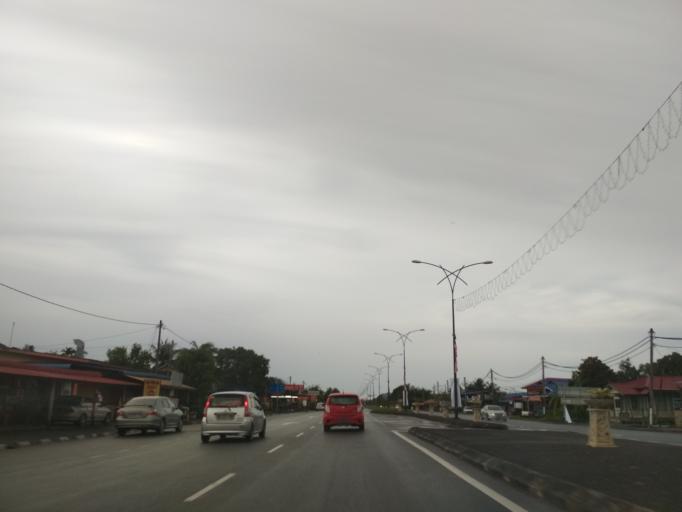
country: MY
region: Perlis
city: Kangar
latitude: 6.4542
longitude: 100.2066
